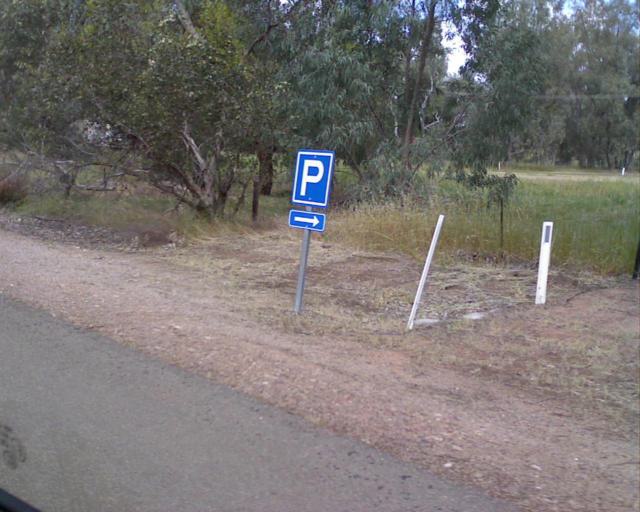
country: AU
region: South Australia
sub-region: Port Pirie City and Dists
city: Solomontown
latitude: -33.0356
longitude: 138.2667
